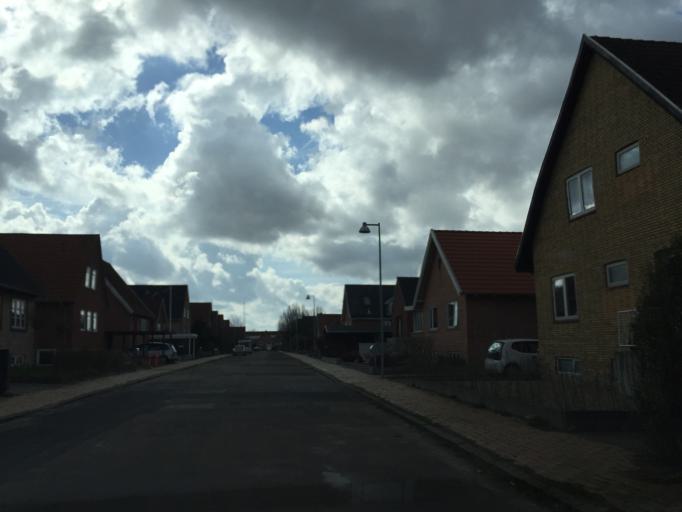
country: DK
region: South Denmark
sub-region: Odense Kommune
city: Stige
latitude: 55.4109
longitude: 10.4153
